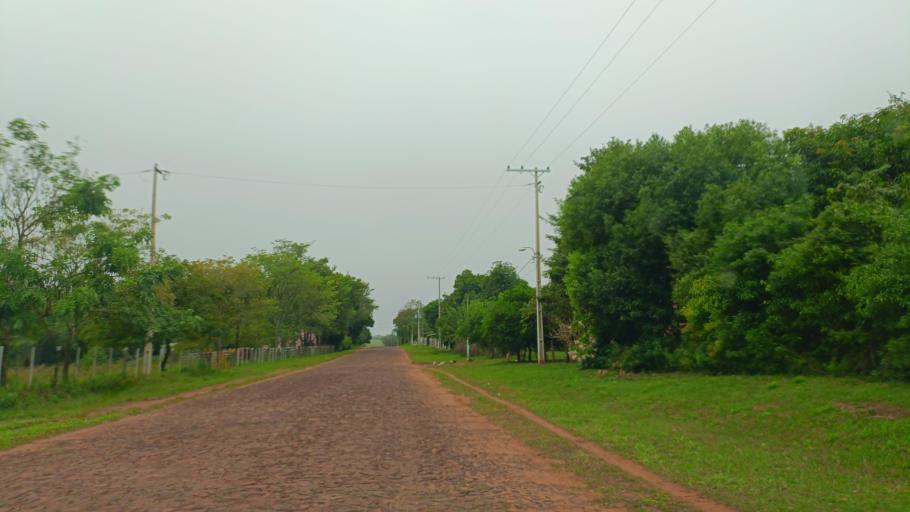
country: PY
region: Misiones
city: Santa Maria
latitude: -26.8625
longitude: -57.0179
